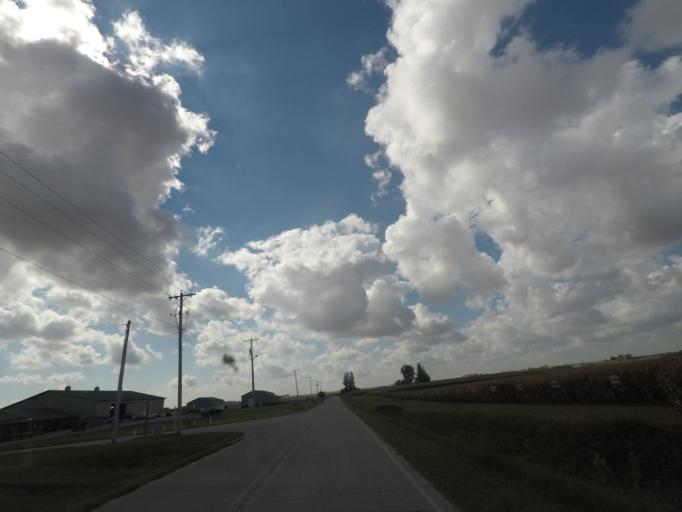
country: US
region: Iowa
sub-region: Story County
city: Nevada
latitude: 42.0075
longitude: -93.3192
